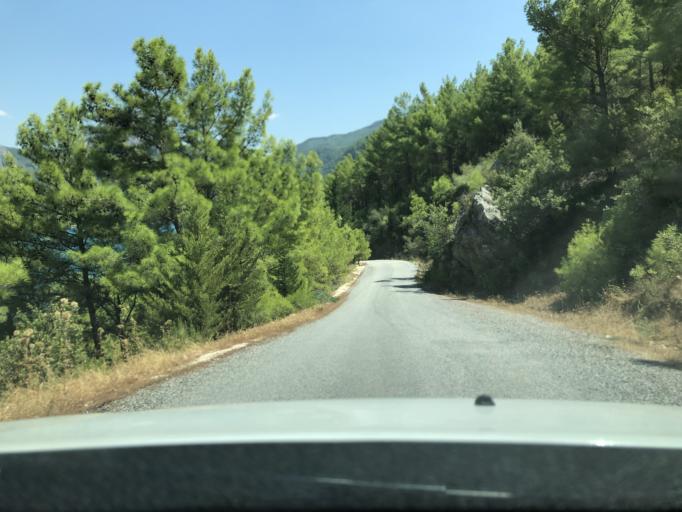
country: TR
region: Antalya
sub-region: Manavgat
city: Manavgat
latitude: 36.9114
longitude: 31.5481
